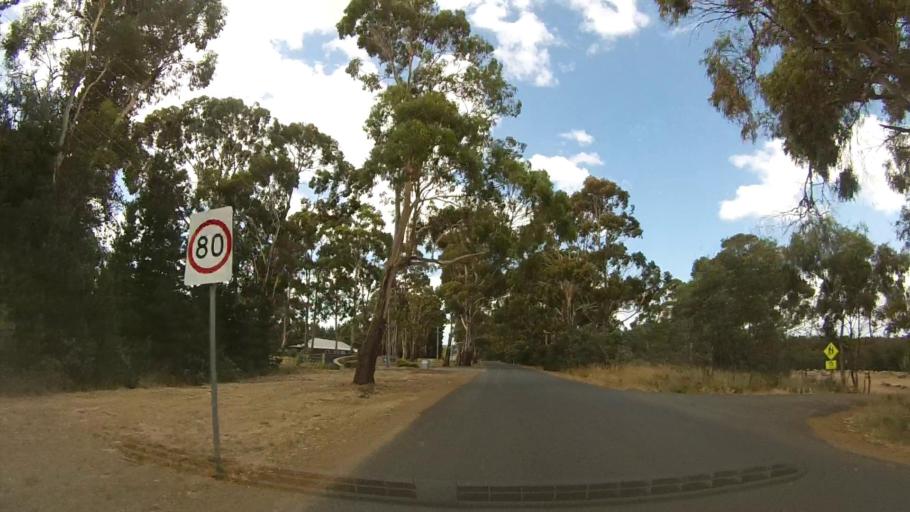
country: AU
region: Tasmania
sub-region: Clarence
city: Seven Mile Beach
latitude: -42.8553
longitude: 147.5121
